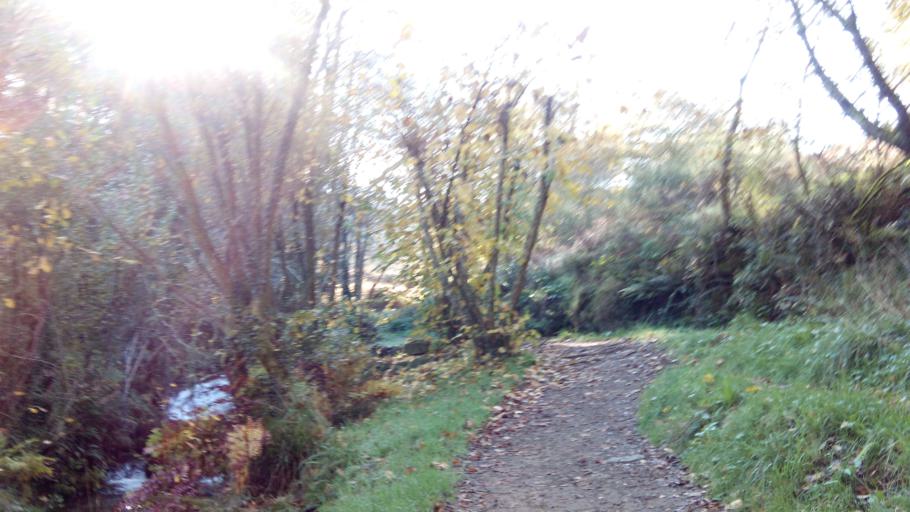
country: ES
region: Galicia
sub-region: Provincia de Pontevedra
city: Meis
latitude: 42.4797
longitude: -8.7406
